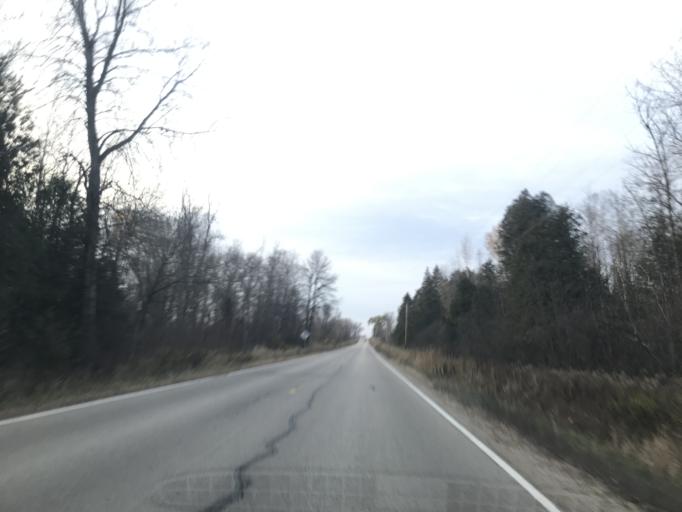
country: US
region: Wisconsin
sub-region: Marinette County
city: Peshtigo
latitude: 45.1044
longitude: -87.7994
